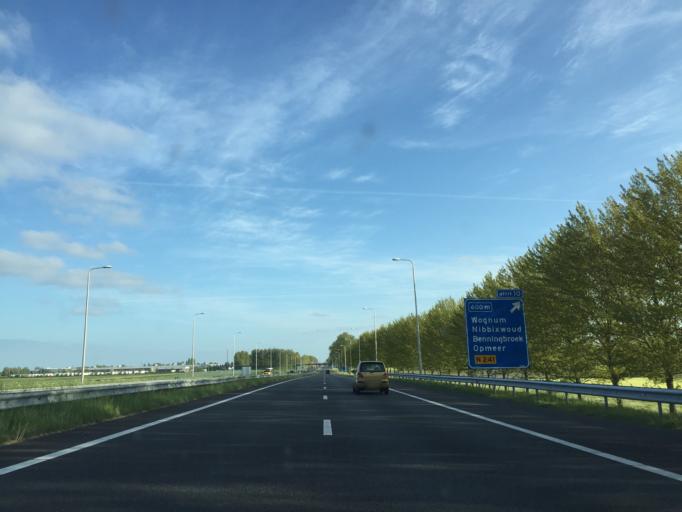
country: NL
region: North Holland
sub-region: Gemeente Hoorn
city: Hoorn
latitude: 52.7015
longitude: 5.0298
